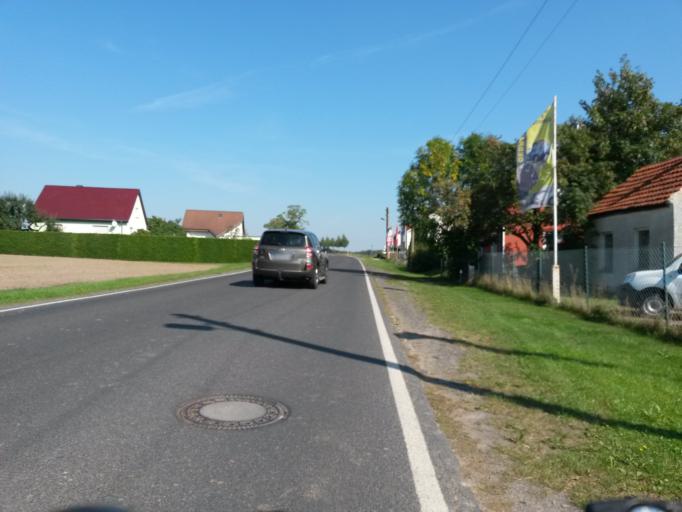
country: DE
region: Brandenburg
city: Templin
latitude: 53.0747
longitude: 13.4381
